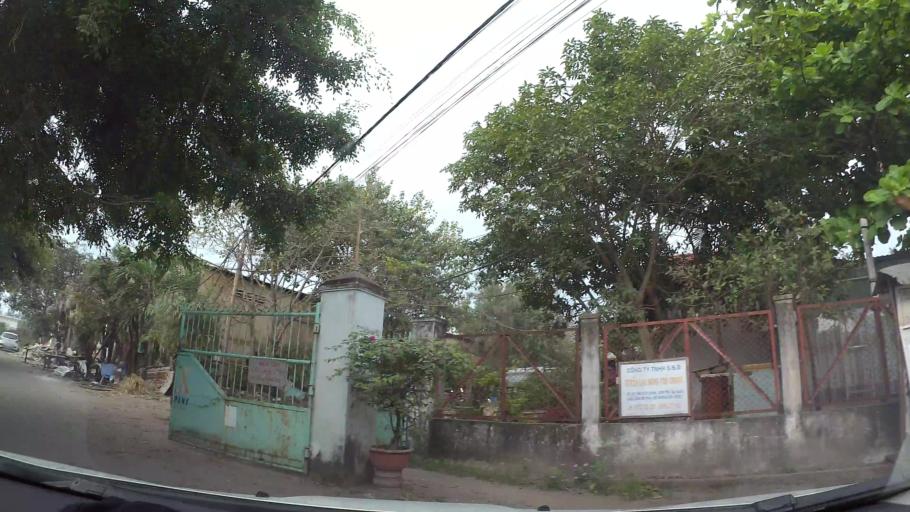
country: VN
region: Da Nang
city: Son Tra
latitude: 16.0794
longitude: 108.2391
